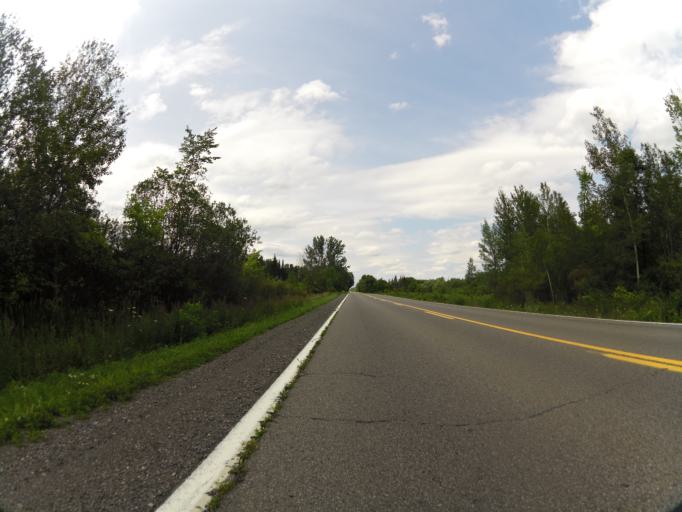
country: CA
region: Ontario
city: Ottawa
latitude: 45.2108
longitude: -75.5975
